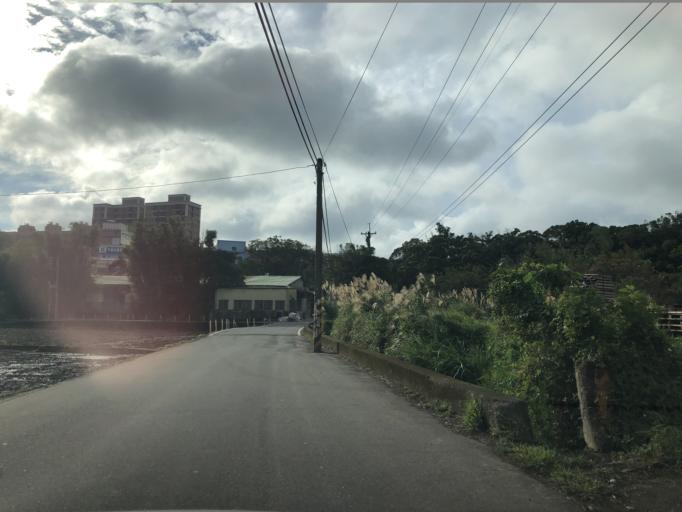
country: TW
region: Taiwan
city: Daxi
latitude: 24.9187
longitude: 121.2572
